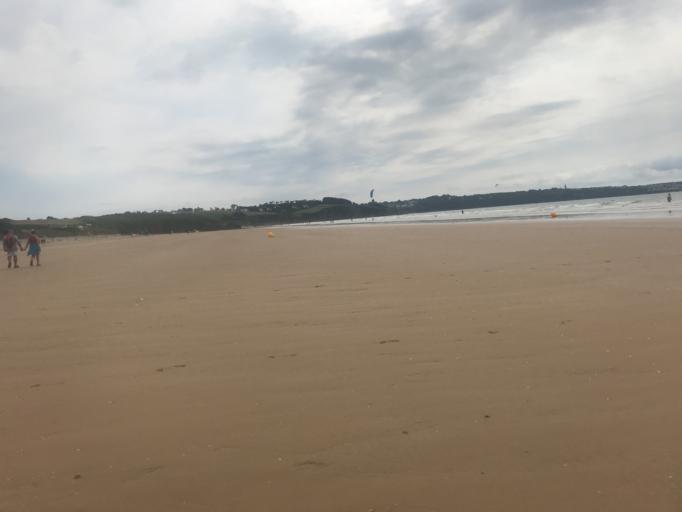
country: FR
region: Brittany
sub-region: Departement du Finistere
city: Douarnenez
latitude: 48.1143
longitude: -4.2833
